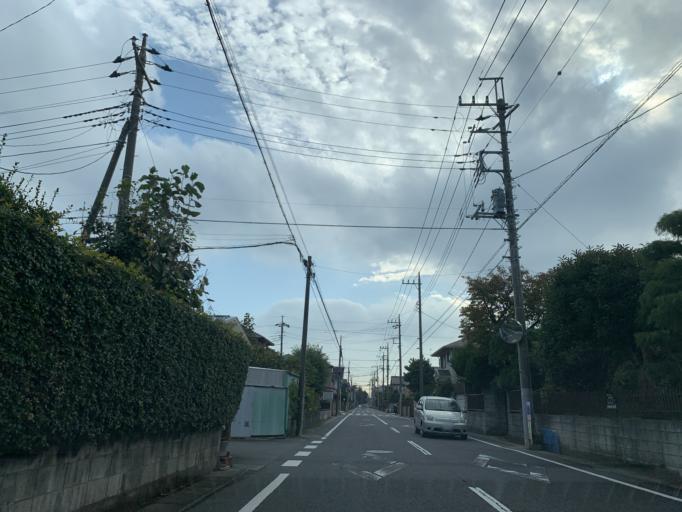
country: JP
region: Chiba
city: Nagareyama
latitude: 35.9026
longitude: 139.9140
